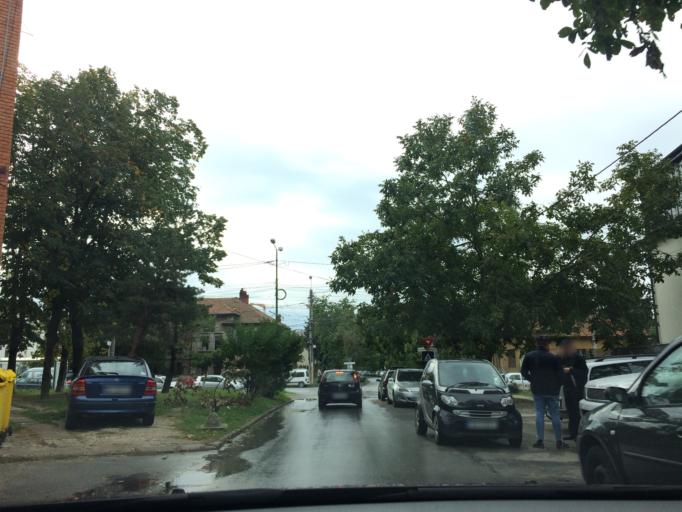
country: RO
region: Timis
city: Timisoara
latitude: 45.7575
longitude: 21.2138
